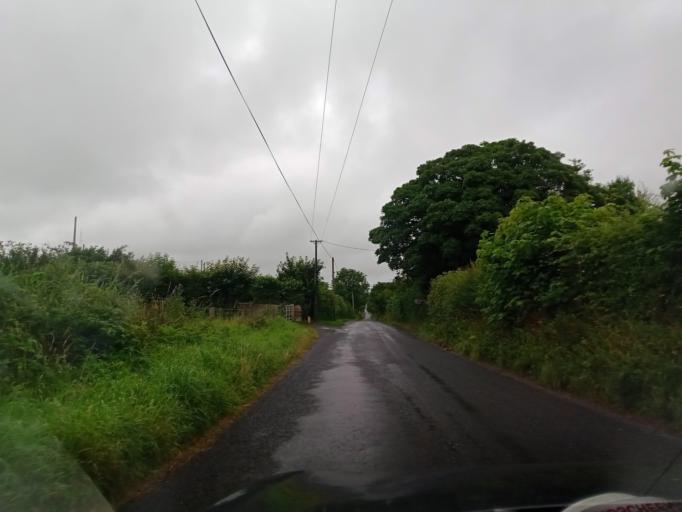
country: IE
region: Leinster
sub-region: Laois
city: Abbeyleix
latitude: 52.9115
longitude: -7.2947
